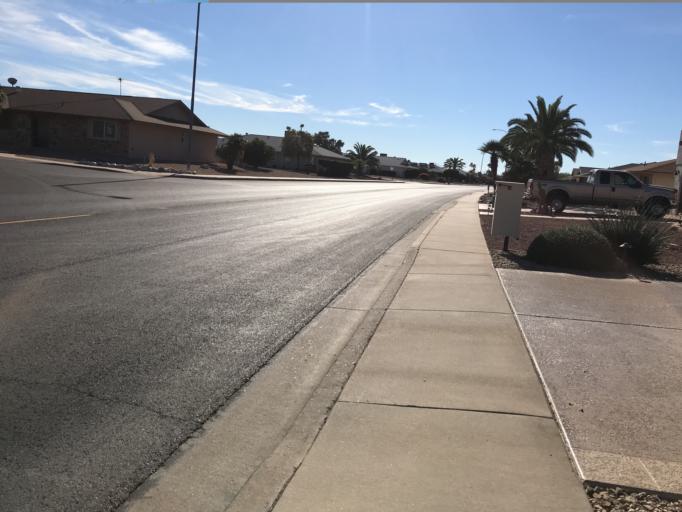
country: US
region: Arizona
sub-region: Maricopa County
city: Sun City West
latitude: 33.6537
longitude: -112.3261
